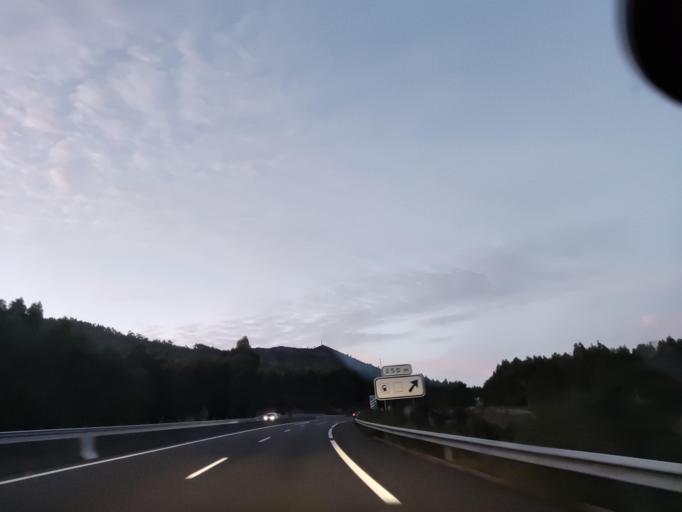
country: ES
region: Galicia
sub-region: Provincia da Coruna
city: Boiro
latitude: 42.6027
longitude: -8.9704
